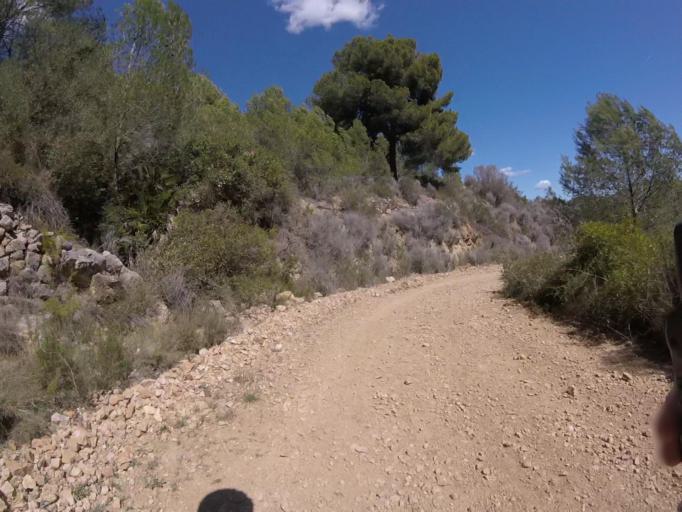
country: ES
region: Valencia
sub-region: Provincia de Castello
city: Cabanes
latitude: 40.1582
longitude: 0.1037
